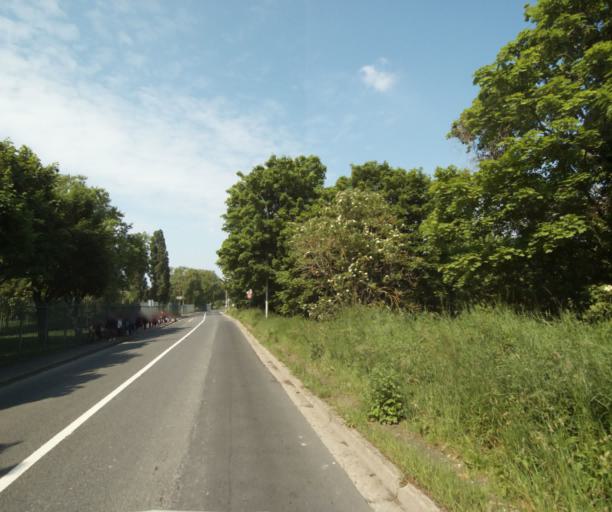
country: FR
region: Ile-de-France
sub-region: Departement du Val-d'Oise
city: Argenteuil
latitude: 48.9563
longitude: 2.2282
